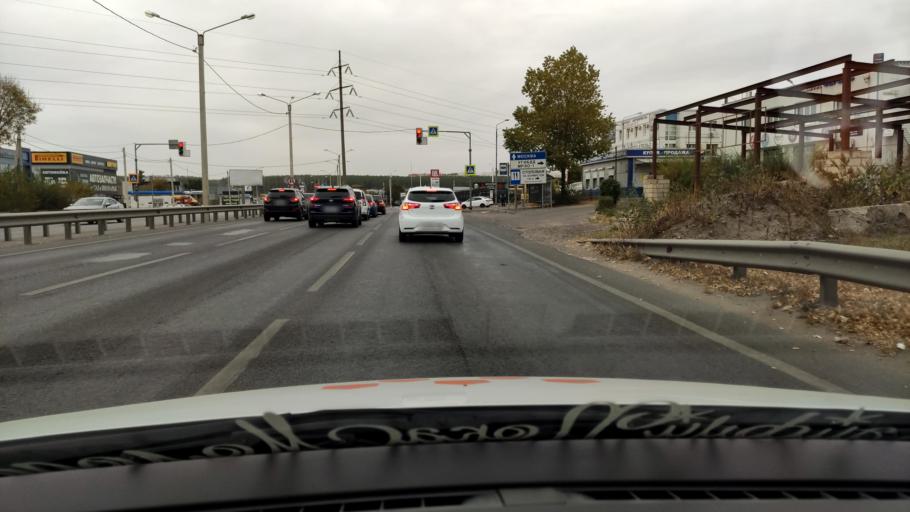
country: RU
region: Voronezj
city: Voronezh
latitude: 51.6659
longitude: 39.1275
